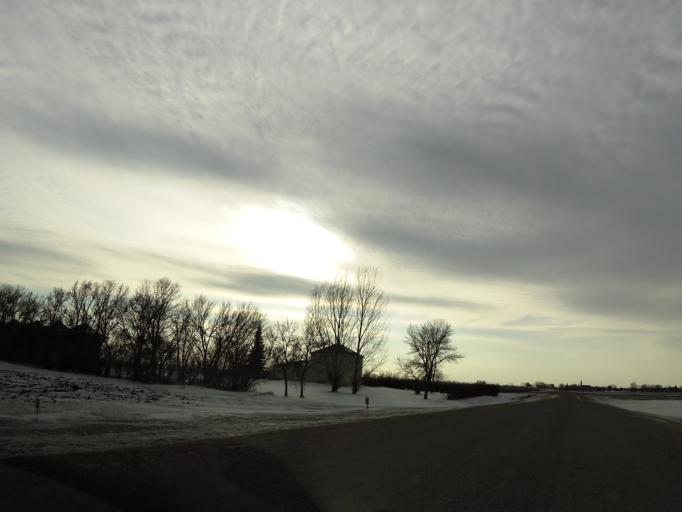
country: US
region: North Dakota
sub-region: Walsh County
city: Grafton
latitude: 48.4265
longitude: -97.2752
